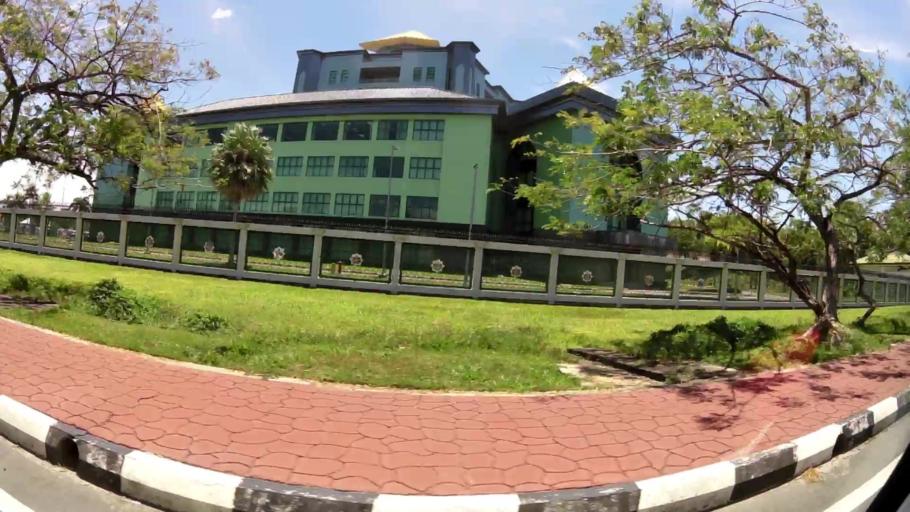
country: BN
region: Brunei and Muara
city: Bandar Seri Begawan
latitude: 4.9255
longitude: 114.9349
